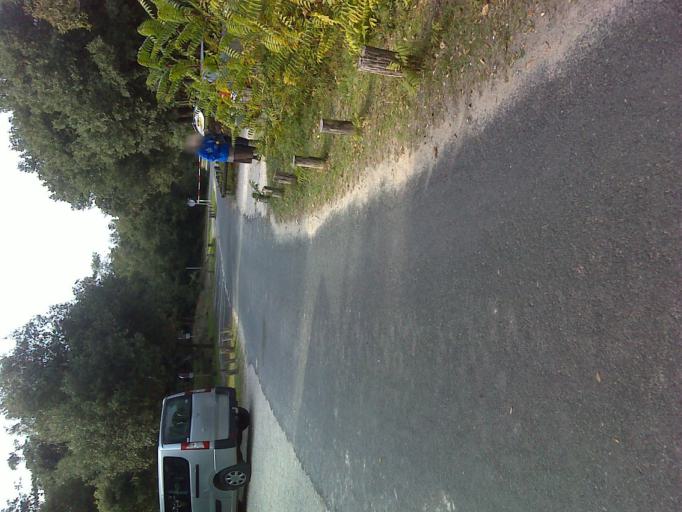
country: FR
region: Poitou-Charentes
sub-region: Departement de la Charente-Maritime
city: Les Mathes
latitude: 45.7287
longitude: -1.2299
